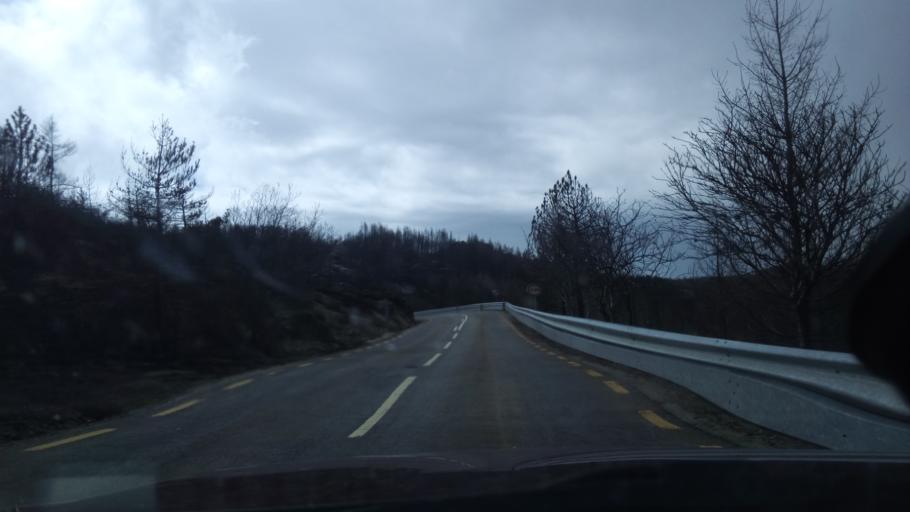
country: PT
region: Guarda
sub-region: Manteigas
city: Manteigas
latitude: 40.4154
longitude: -7.5831
